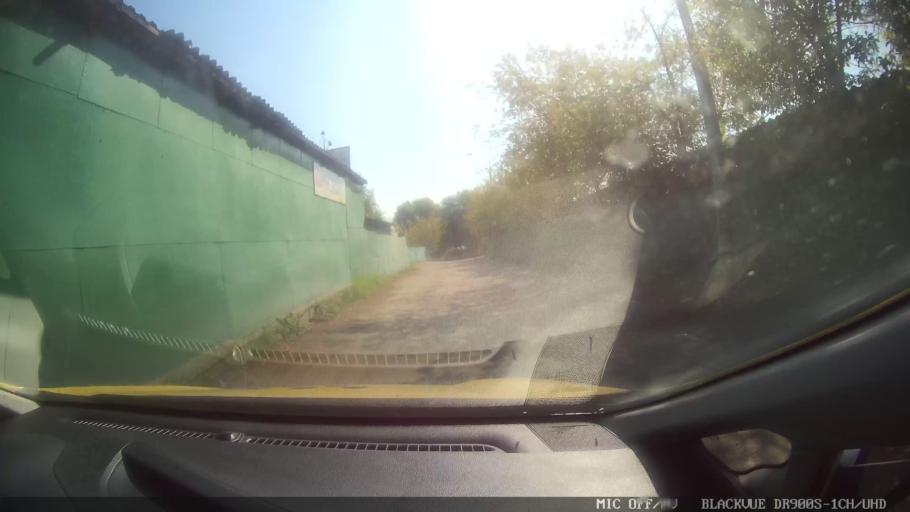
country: RU
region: Moscow
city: Bibirevo
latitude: 55.8802
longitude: 37.6062
